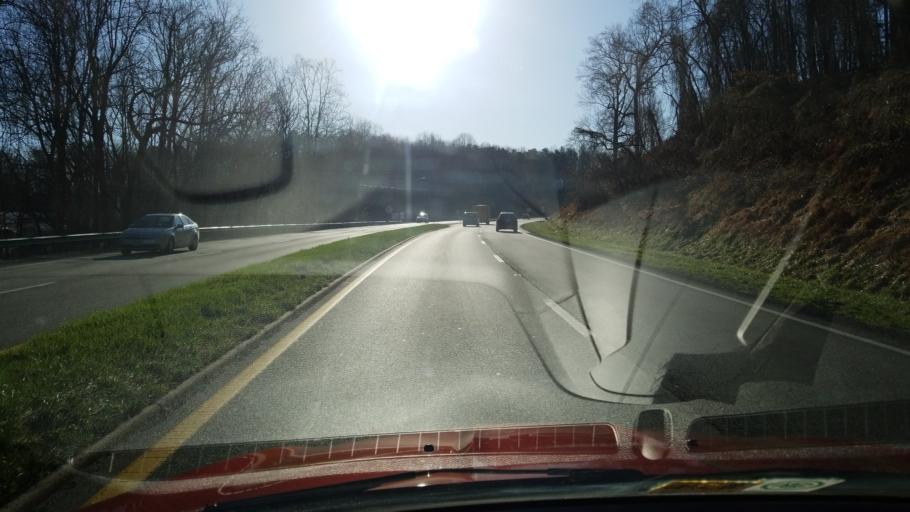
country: US
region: Virginia
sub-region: Roanoke County
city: Narrows
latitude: 37.1121
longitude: -79.9496
